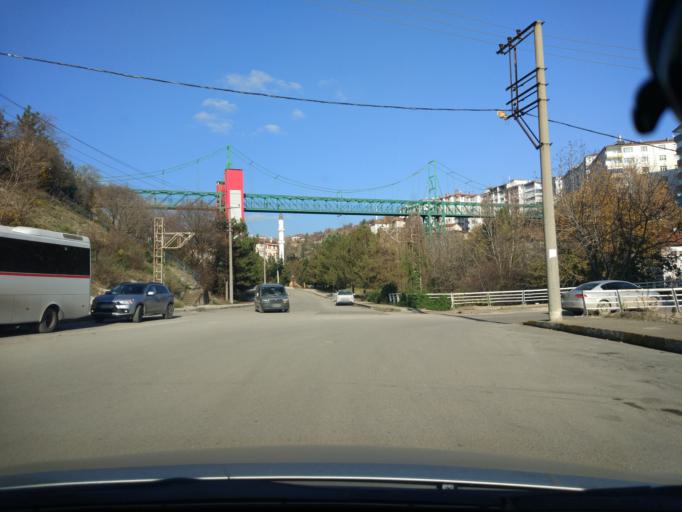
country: TR
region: Karabuk
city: Karabuk
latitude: 41.2064
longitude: 32.6239
